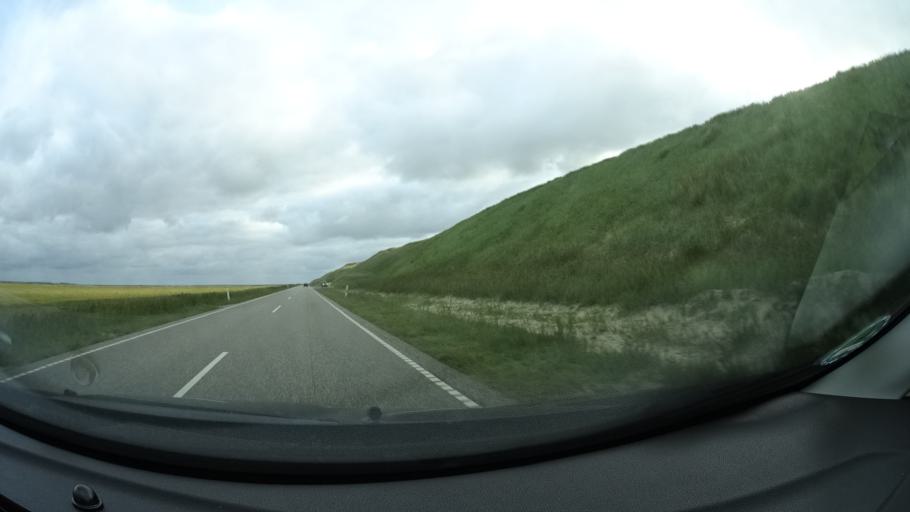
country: DK
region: Central Jutland
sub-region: Lemvig Kommune
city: Harboore
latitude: 56.4393
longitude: 8.1246
